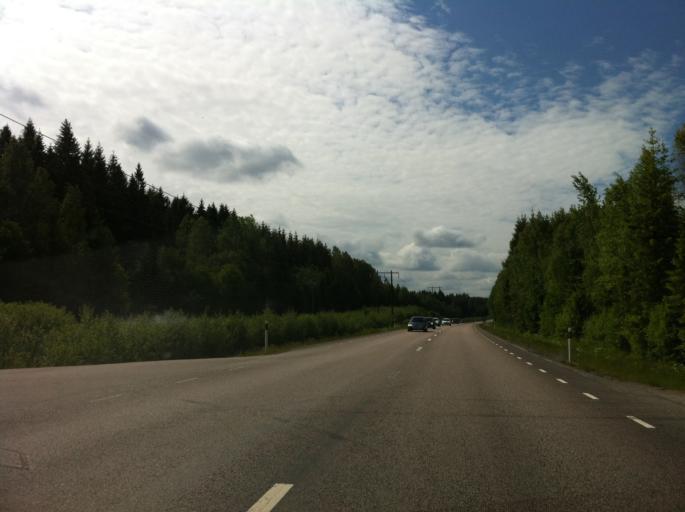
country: SE
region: Vaermland
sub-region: Karlstads Kommun
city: Edsvalla
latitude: 59.4311
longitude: 13.1990
